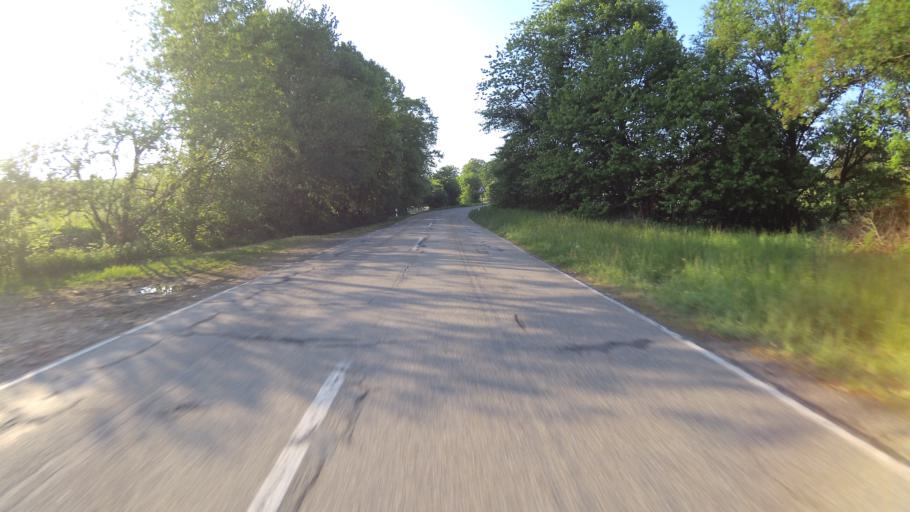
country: DE
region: Rheinland-Pfalz
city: Contwig
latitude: 49.2222
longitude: 7.4170
